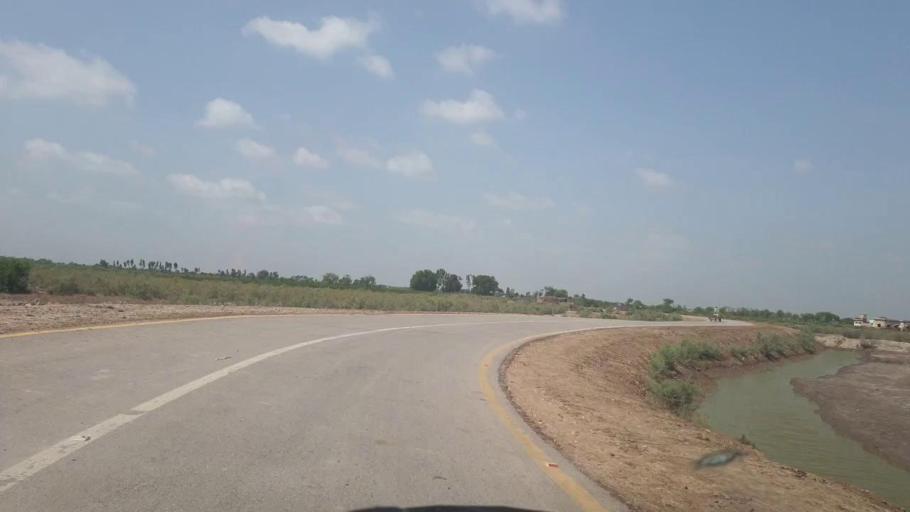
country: PK
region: Sindh
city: Berani
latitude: 25.6933
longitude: 68.9320
